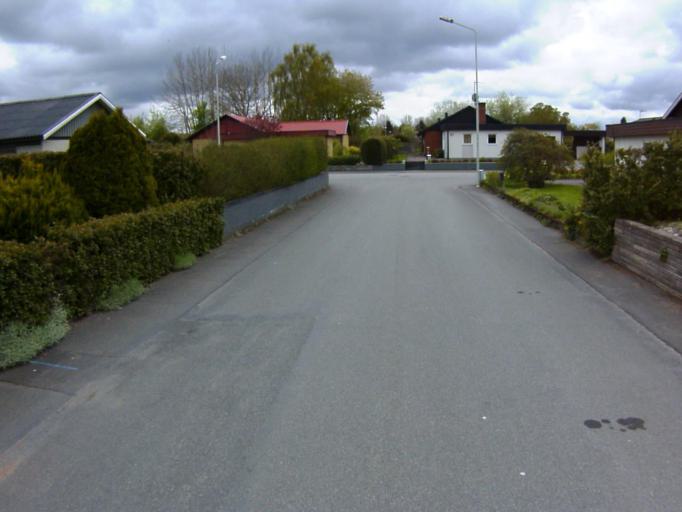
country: SE
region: Skane
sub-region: Kristianstads Kommun
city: Kristianstad
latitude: 56.0497
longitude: 14.1826
